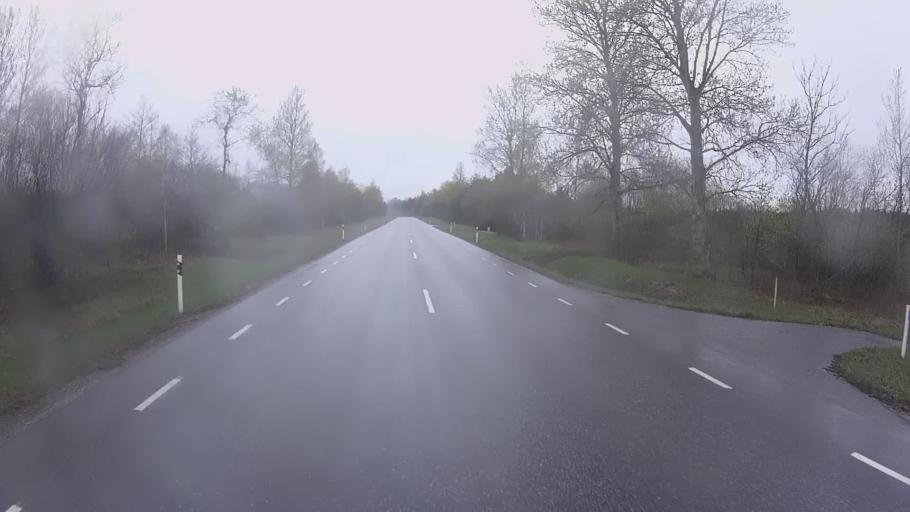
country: EE
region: Hiiumaa
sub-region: Kaerdla linn
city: Kardla
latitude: 58.9904
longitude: 22.5185
